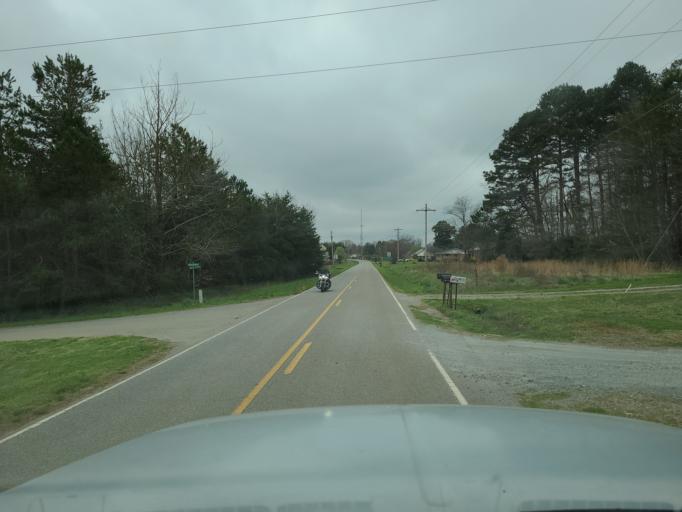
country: US
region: North Carolina
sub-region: Cleveland County
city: Shelby
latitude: 35.4272
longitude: -81.6397
